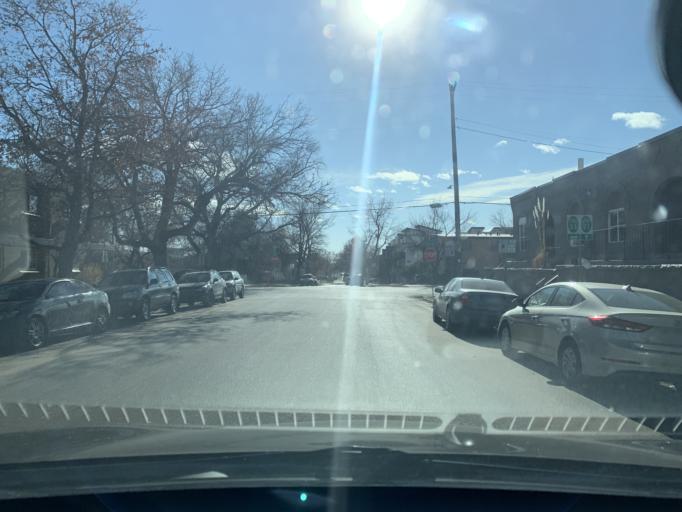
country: US
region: Colorado
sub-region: Jefferson County
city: Edgewater
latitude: 39.7517
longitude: -105.0237
